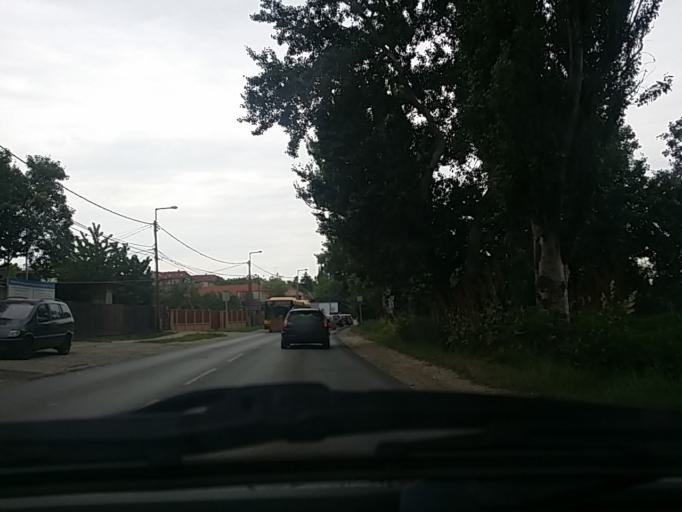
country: HU
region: Pest
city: Pilisborosjeno
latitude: 47.5866
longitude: 18.9957
